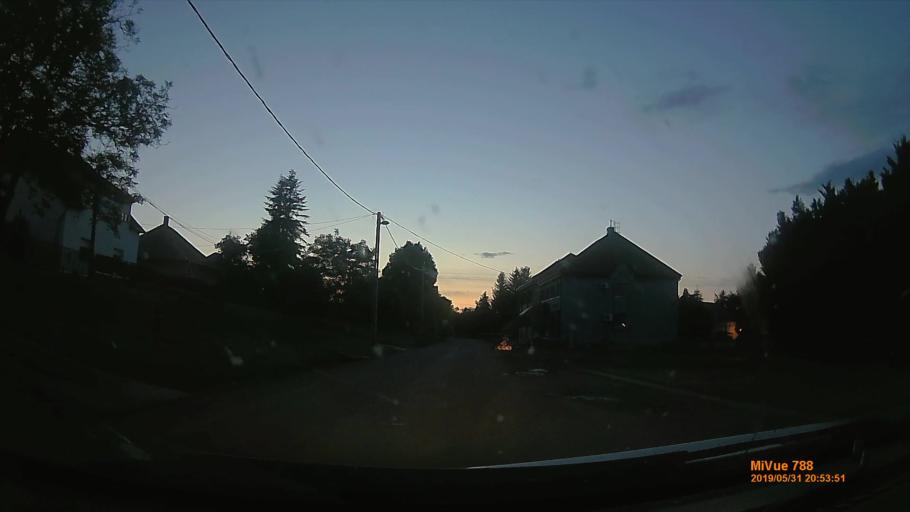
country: HU
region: Nograd
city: Nagyoroszi
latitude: 48.0503
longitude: 19.0479
